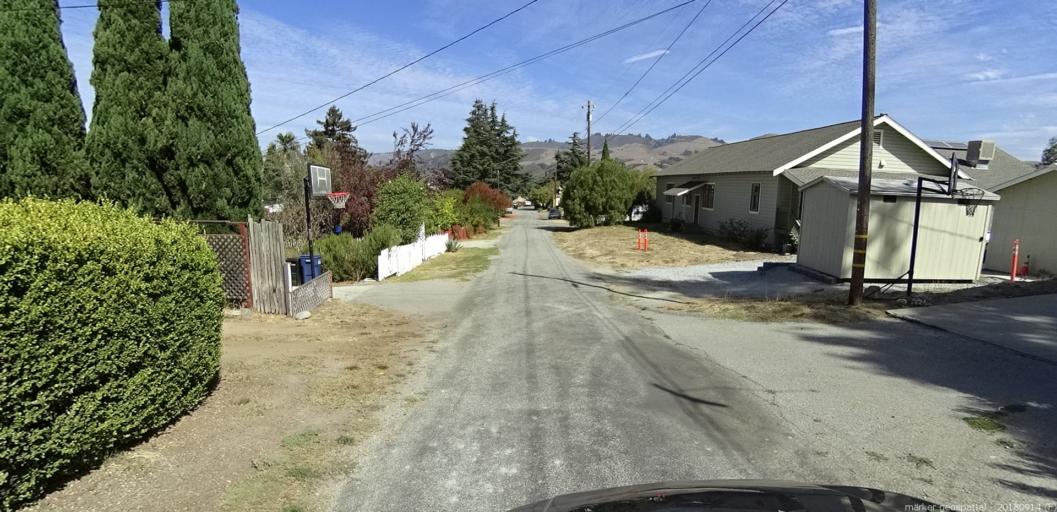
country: US
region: California
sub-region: San Benito County
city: Aromas
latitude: 36.8868
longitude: -121.6440
